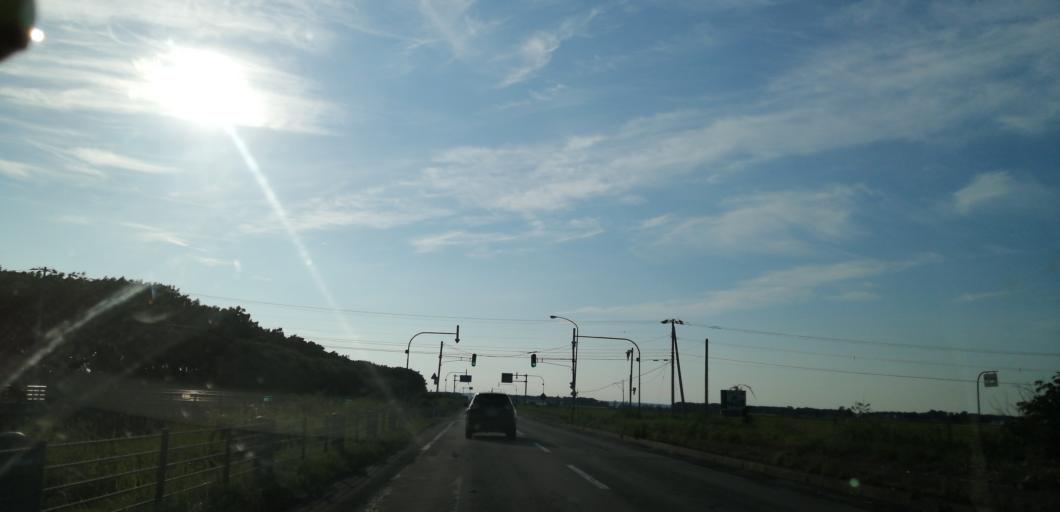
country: JP
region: Hokkaido
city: Kitahiroshima
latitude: 42.9803
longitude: 141.6347
